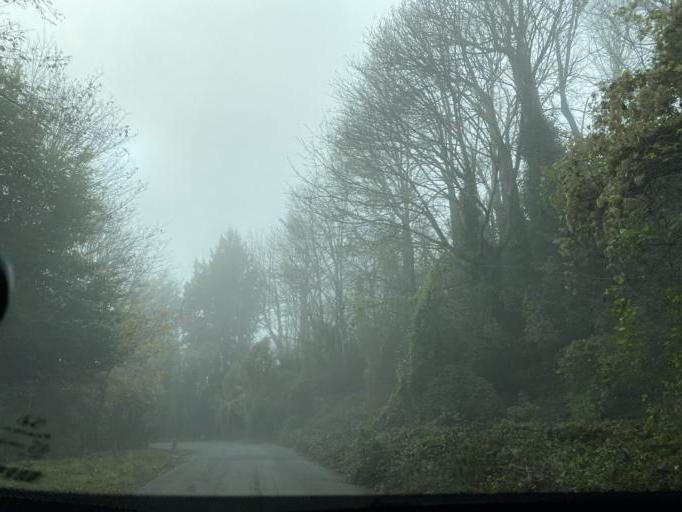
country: US
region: Washington
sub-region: King County
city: Seattle
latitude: 47.6527
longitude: -122.4162
